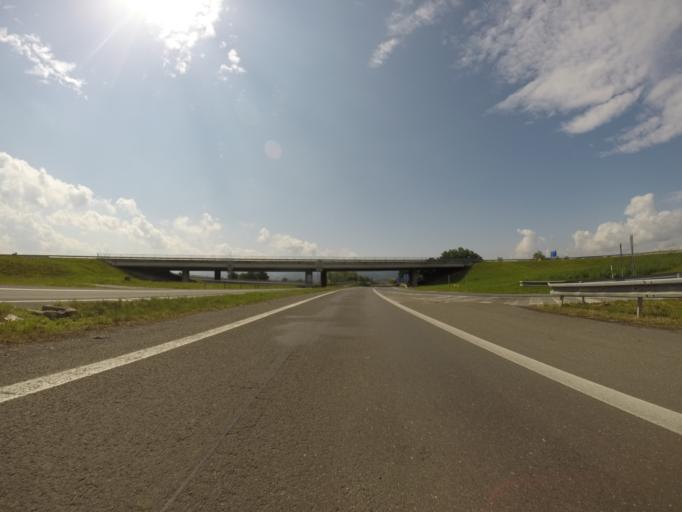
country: SK
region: Banskobystricky
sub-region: Okres Banska Bystrica
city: Zvolen
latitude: 48.5994
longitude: 19.1082
